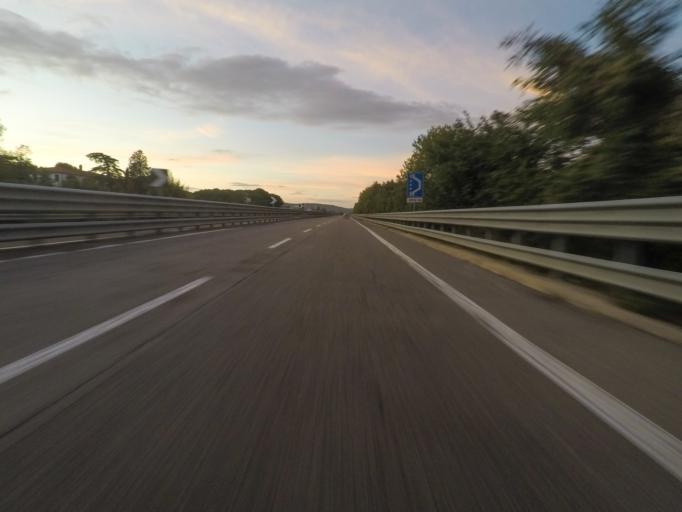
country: IT
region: Tuscany
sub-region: Provincia di Siena
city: Sinalunga
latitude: 43.2321
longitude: 11.7302
